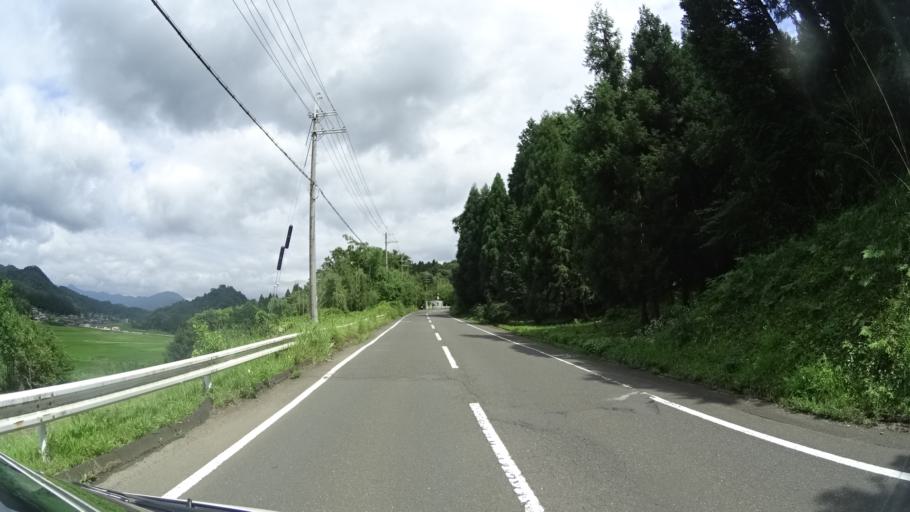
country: JP
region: Kyoto
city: Ayabe
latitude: 35.3523
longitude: 135.2719
